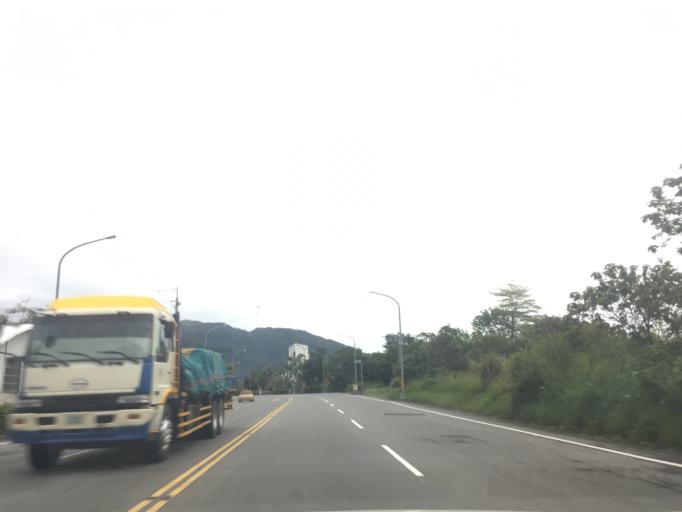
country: TW
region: Taiwan
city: Taitung City
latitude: 22.7453
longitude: 121.0570
